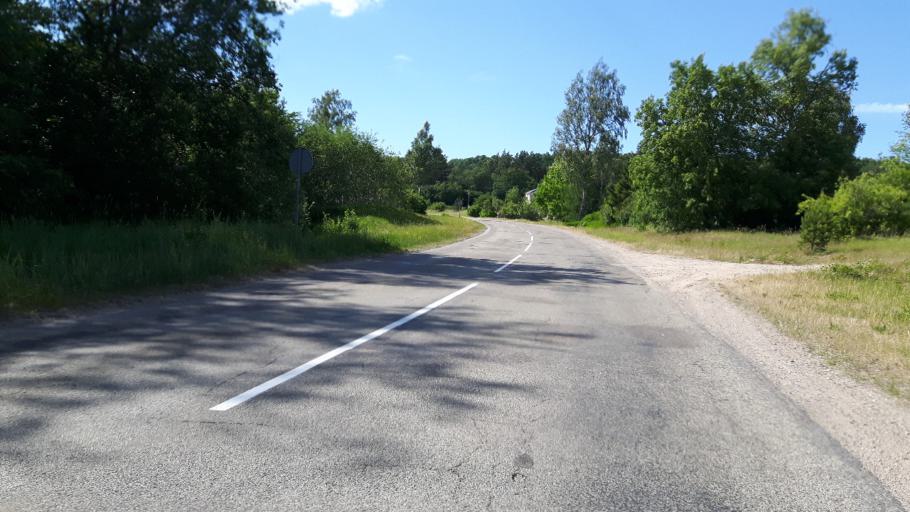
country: LV
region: Talsu Rajons
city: Sabile
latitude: 57.0846
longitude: 22.5243
